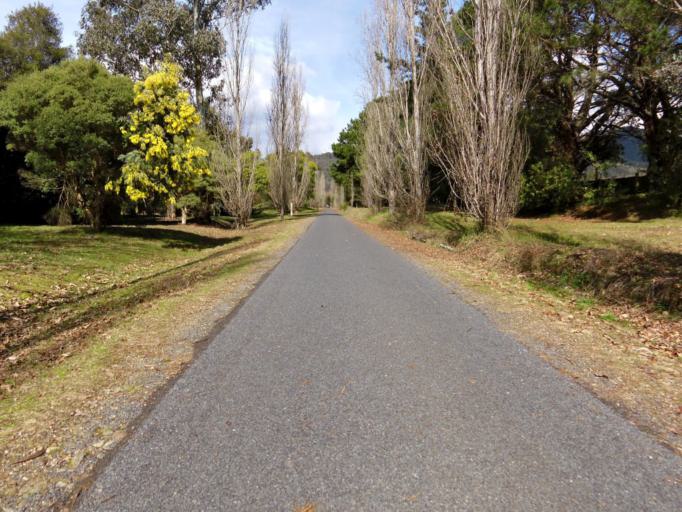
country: AU
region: Victoria
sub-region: Alpine
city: Mount Beauty
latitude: -36.7201
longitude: 146.9448
